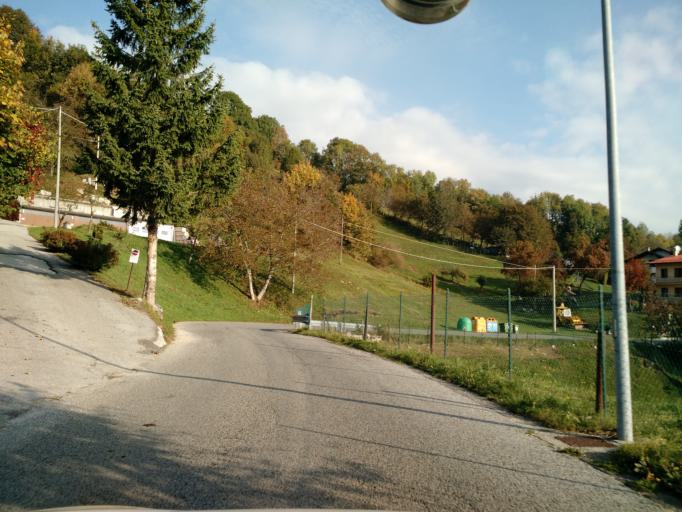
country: IT
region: Veneto
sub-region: Provincia di Vicenza
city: Foza
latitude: 45.8645
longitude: 11.6165
